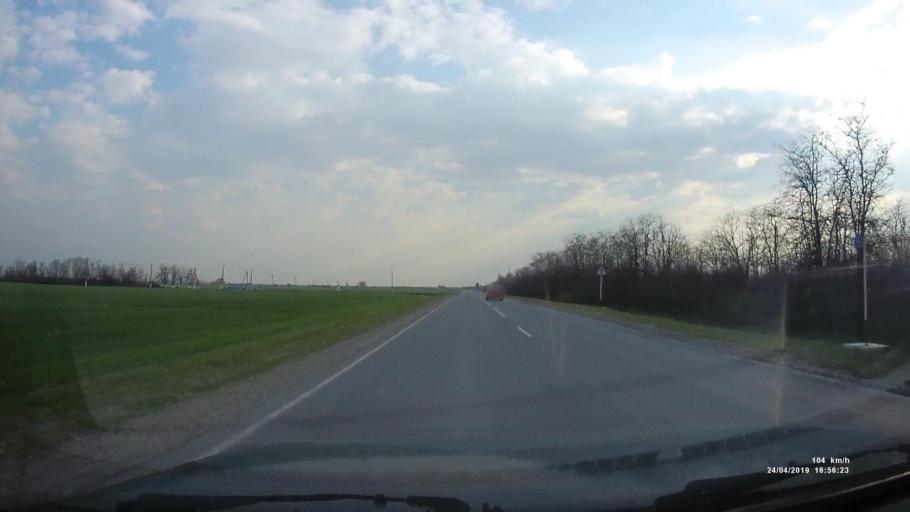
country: RU
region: Rostov
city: Proletarsk
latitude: 46.6524
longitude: 41.6788
